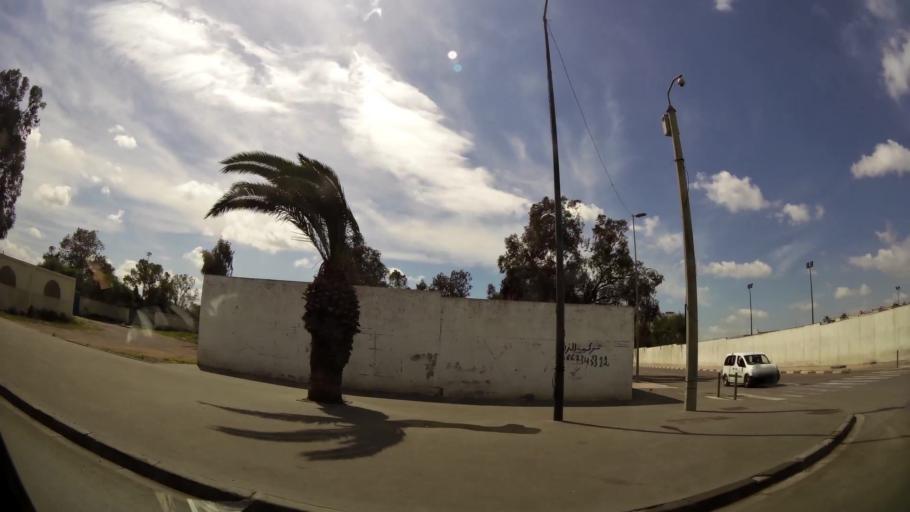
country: MA
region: Grand Casablanca
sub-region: Casablanca
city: Casablanca
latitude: 33.6003
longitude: -7.5626
